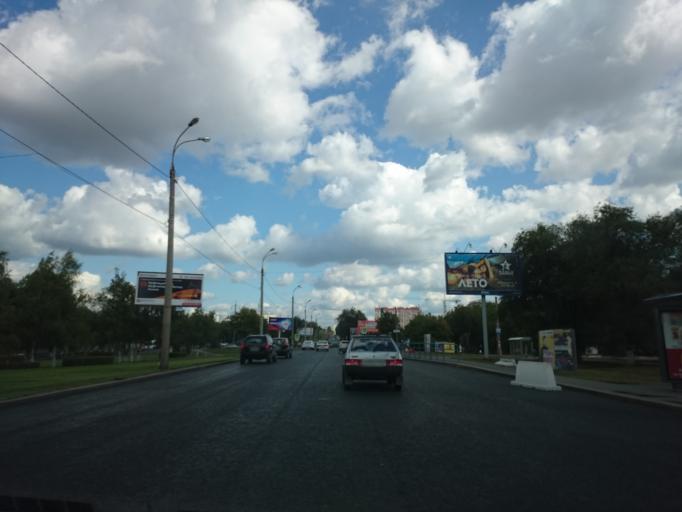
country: RU
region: Samara
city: Samara
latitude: 53.2233
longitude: 50.1696
